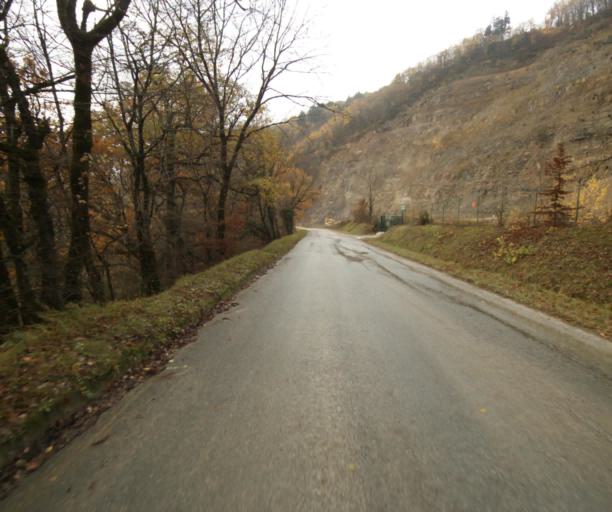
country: FR
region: Limousin
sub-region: Departement de la Correze
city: Cornil
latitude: 45.1951
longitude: 1.6516
